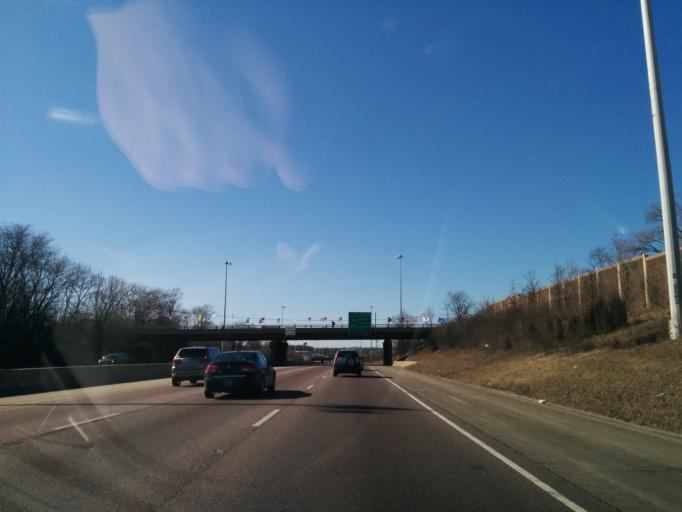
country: US
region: Illinois
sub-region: Cook County
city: Indian Head Park
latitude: 41.7609
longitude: -87.8854
